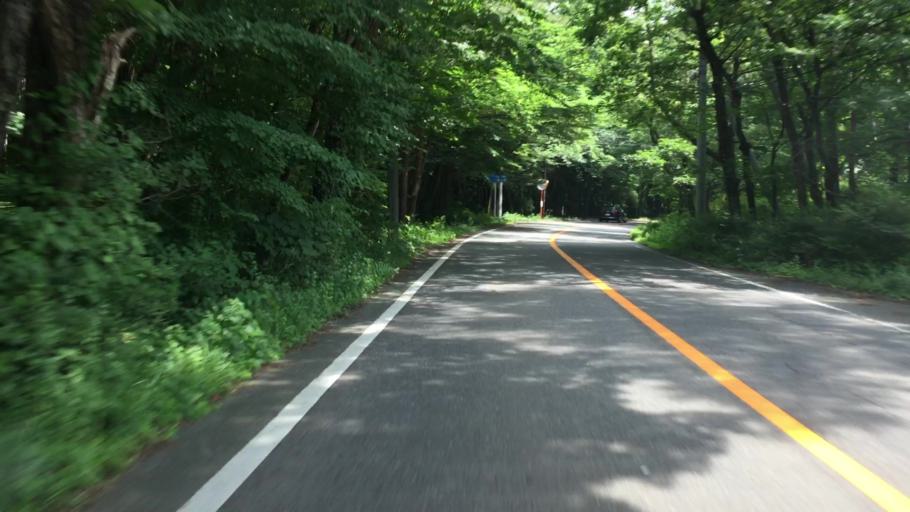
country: JP
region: Tochigi
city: Kuroiso
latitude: 37.0423
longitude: 139.9418
